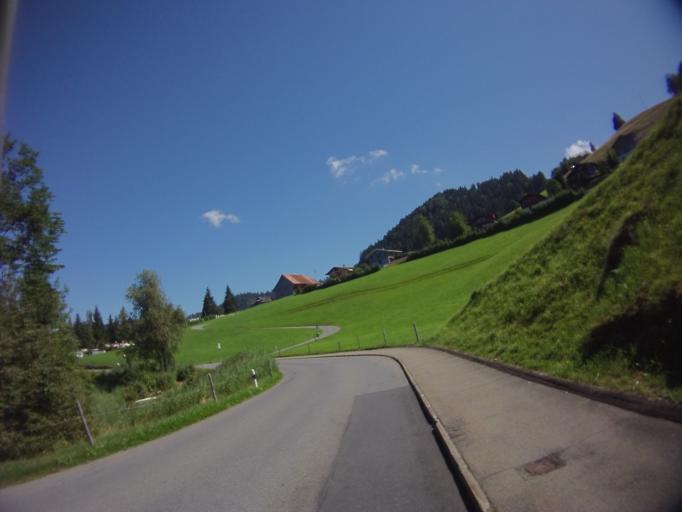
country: CH
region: Schwyz
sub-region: Bezirk Einsiedeln
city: Einsiedeln
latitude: 47.1367
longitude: 8.7916
